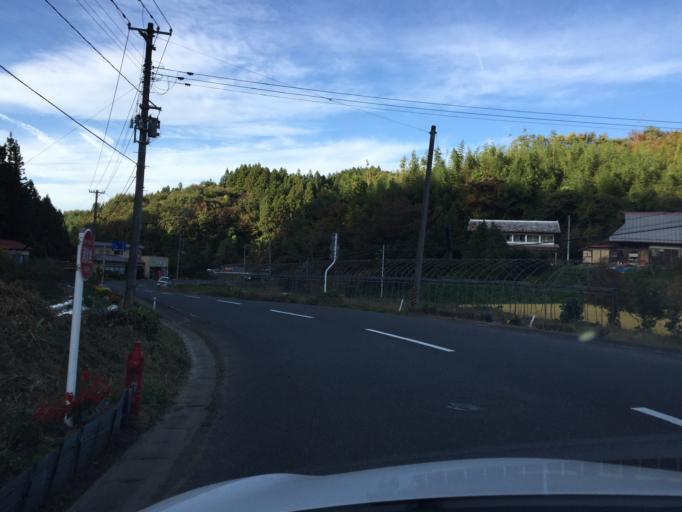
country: JP
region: Fukushima
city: Ishikawa
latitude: 37.2027
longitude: 140.5867
